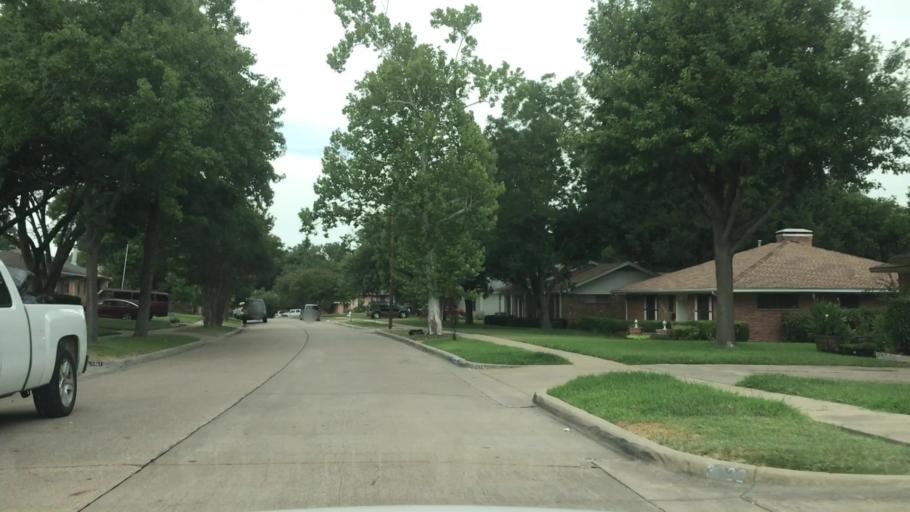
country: US
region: Texas
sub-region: Dallas County
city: Garland
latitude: 32.8764
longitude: -96.6412
